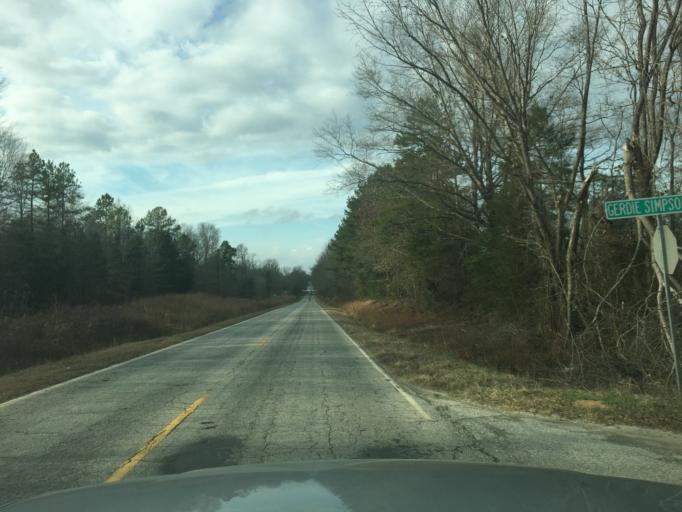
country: US
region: South Carolina
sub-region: Abbeville County
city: Due West
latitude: 34.3473
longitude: -82.4978
